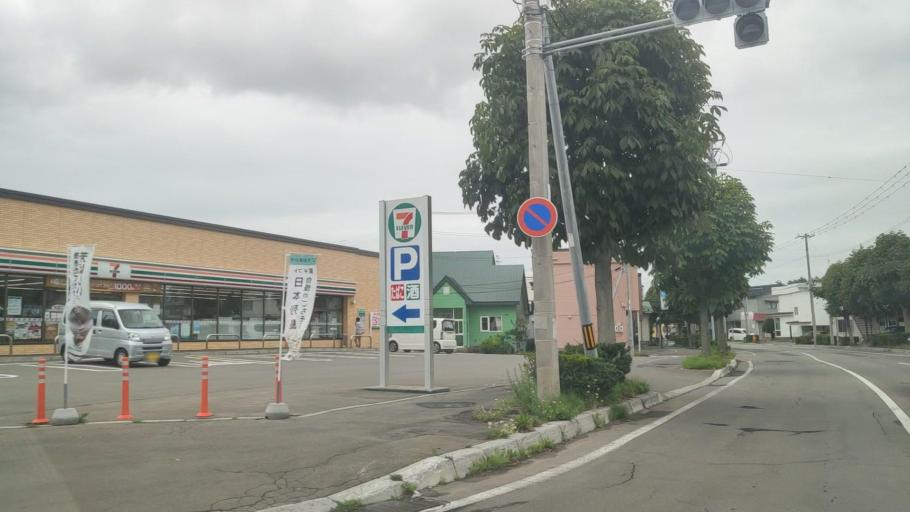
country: JP
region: Hokkaido
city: Hakodate
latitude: 41.7984
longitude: 140.7622
